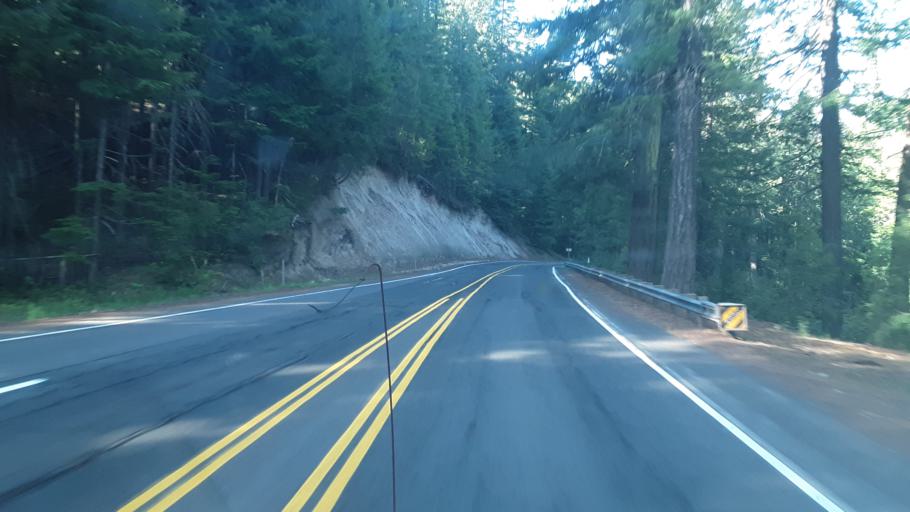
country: US
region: Oregon
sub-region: Jackson County
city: Shady Cove
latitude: 42.9208
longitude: -122.4296
